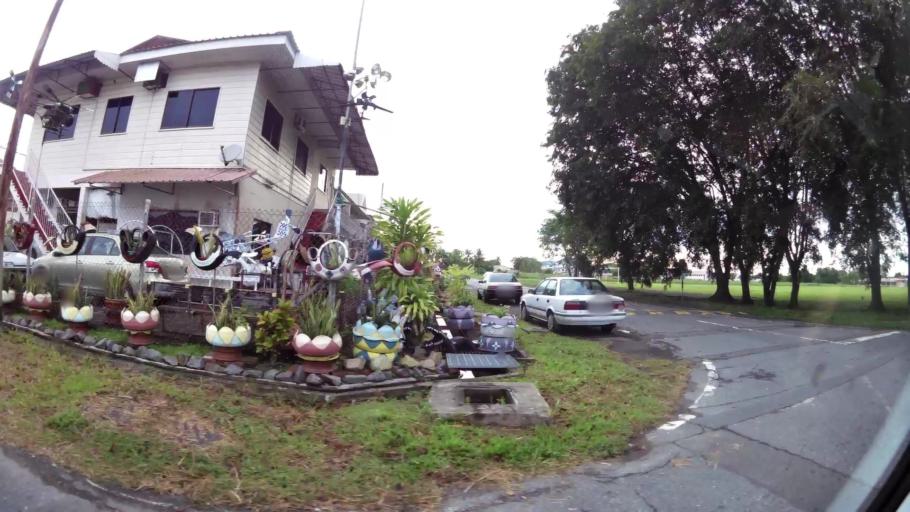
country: BN
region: Belait
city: Seria
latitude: 4.6101
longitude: 114.3316
